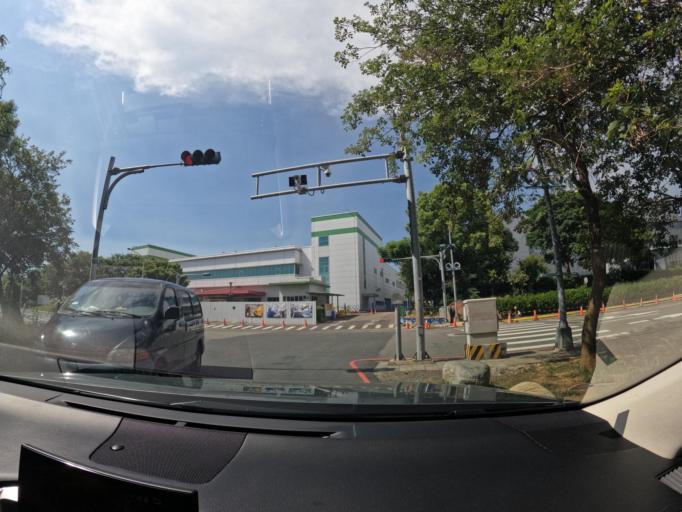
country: TW
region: Taiwan
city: Fengyuan
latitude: 24.3151
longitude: 120.7285
